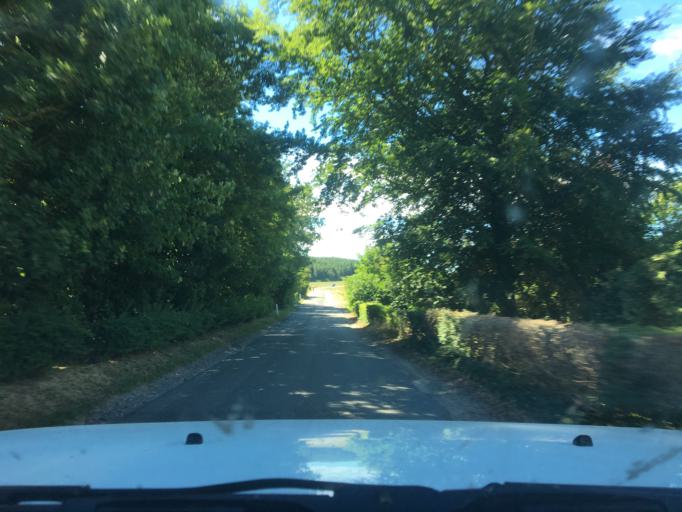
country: DK
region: Central Jutland
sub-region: Syddjurs Kommune
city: Ronde
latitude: 56.3417
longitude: 10.4349
